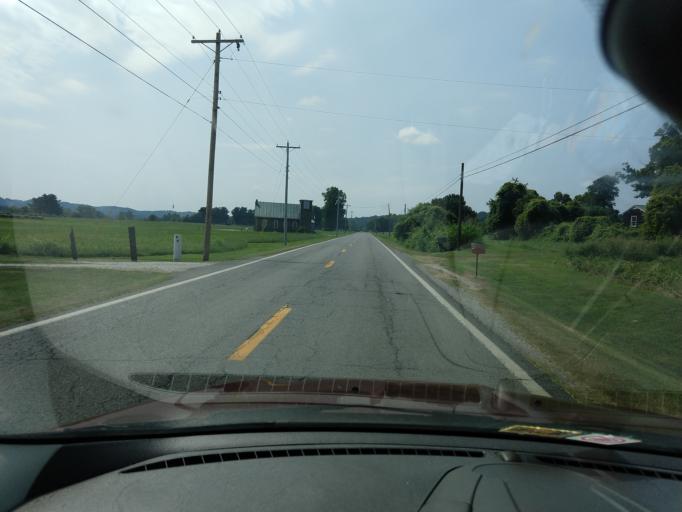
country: US
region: West Virginia
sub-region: Mason County
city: New Haven
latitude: 38.9461
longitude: -81.9202
